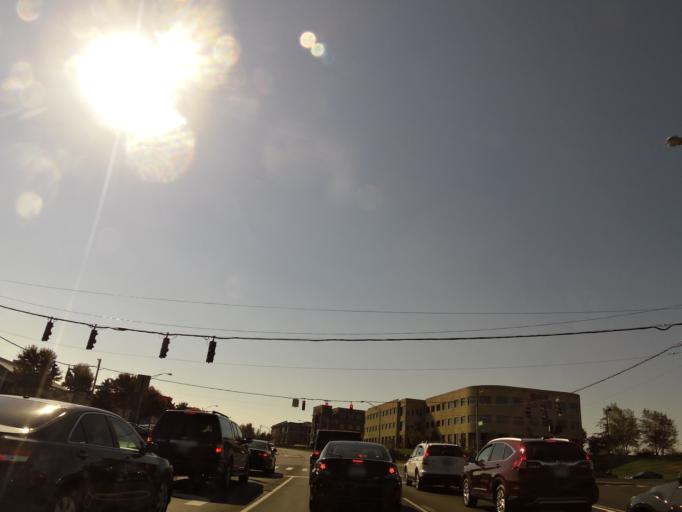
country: US
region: Kentucky
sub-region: Fayette County
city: Lexington-Fayette
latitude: 38.0165
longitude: -84.4197
